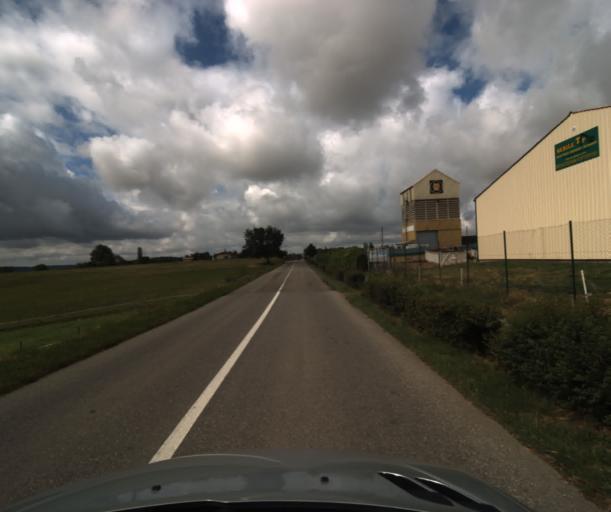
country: FR
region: Midi-Pyrenees
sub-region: Departement du Tarn-et-Garonne
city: Lavit
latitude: 43.9652
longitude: 0.9344
